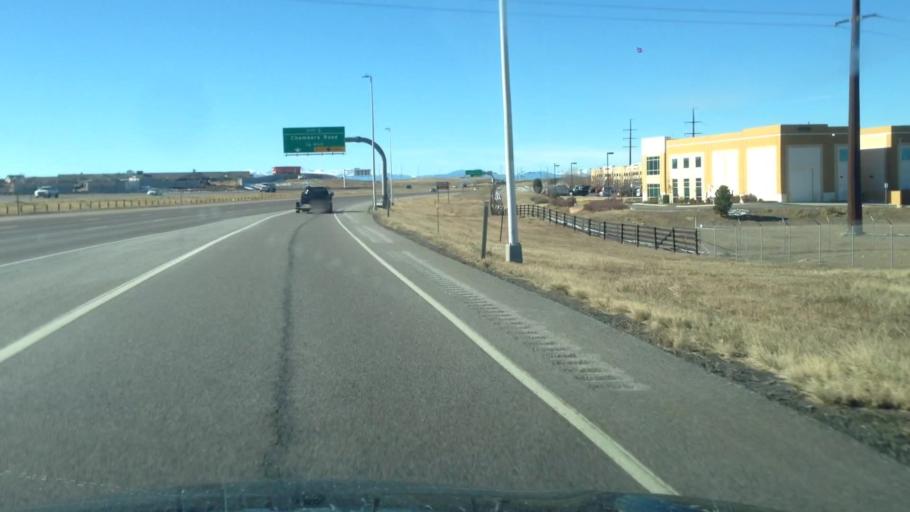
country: US
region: Colorado
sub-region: Douglas County
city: Stonegate
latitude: 39.5497
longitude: -104.7978
